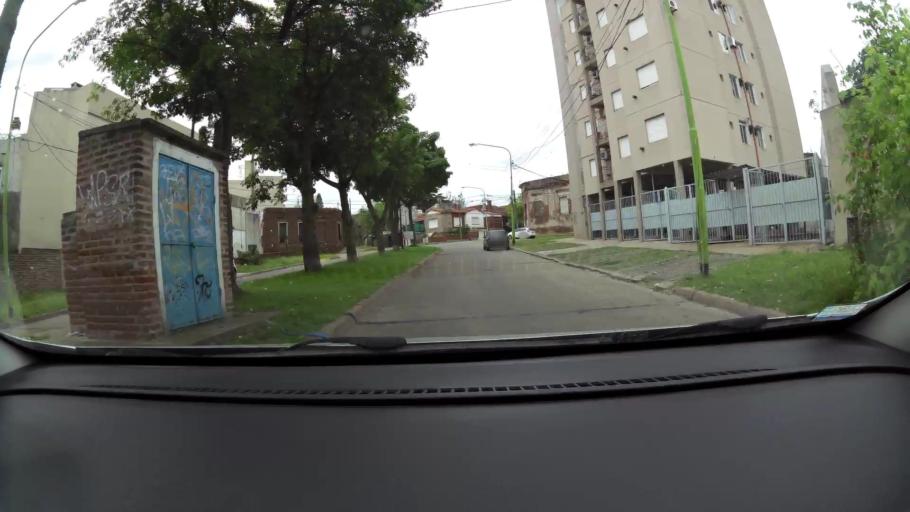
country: AR
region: Buenos Aires
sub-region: Partido de Campana
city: Campana
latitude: -34.1611
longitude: -58.9561
